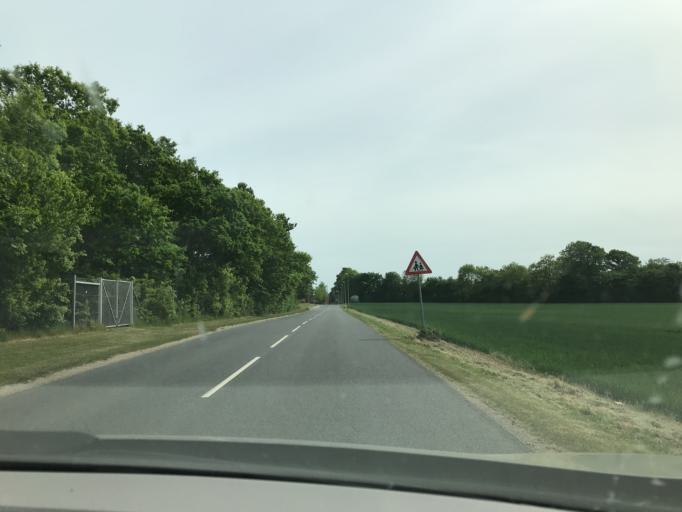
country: DK
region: Central Jutland
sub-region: Norddjurs Kommune
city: Allingabro
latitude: 56.5101
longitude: 10.3325
